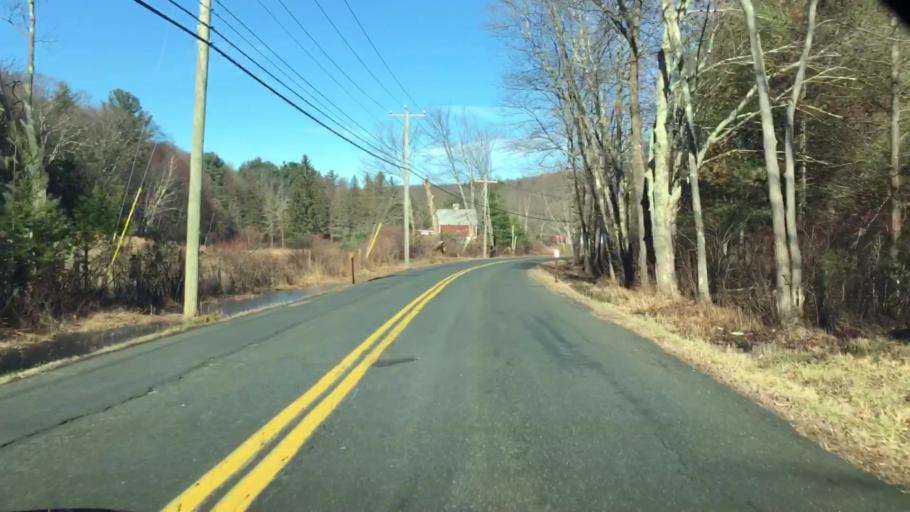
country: US
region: Connecticut
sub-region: Tolland County
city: Crystal Lake
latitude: 41.9291
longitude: -72.3883
